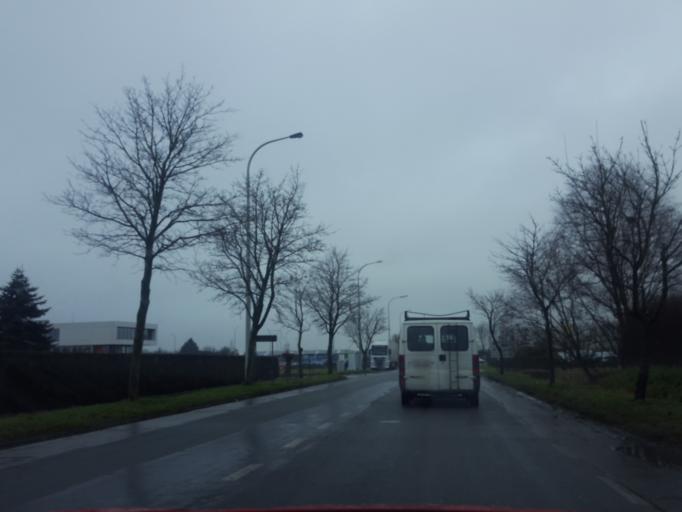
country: BE
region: Flanders
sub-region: Provincie West-Vlaanderen
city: Ieper
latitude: 50.8692
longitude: 2.8883
